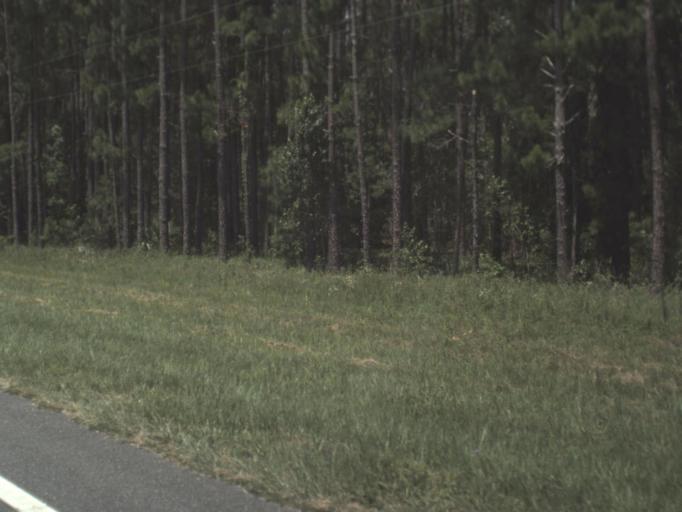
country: US
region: Florida
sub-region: Alachua County
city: High Springs
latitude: 29.9260
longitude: -82.8602
